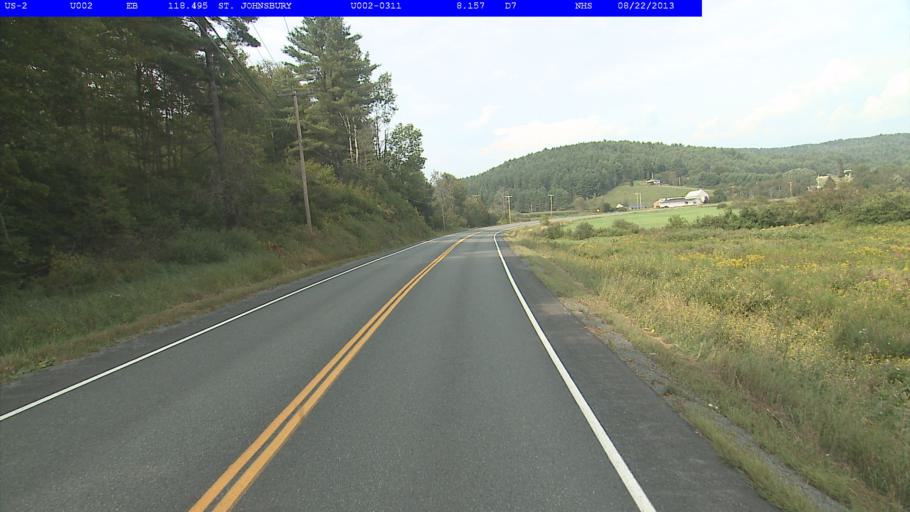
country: US
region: Vermont
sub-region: Caledonia County
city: St Johnsbury
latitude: 44.4456
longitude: -71.9445
